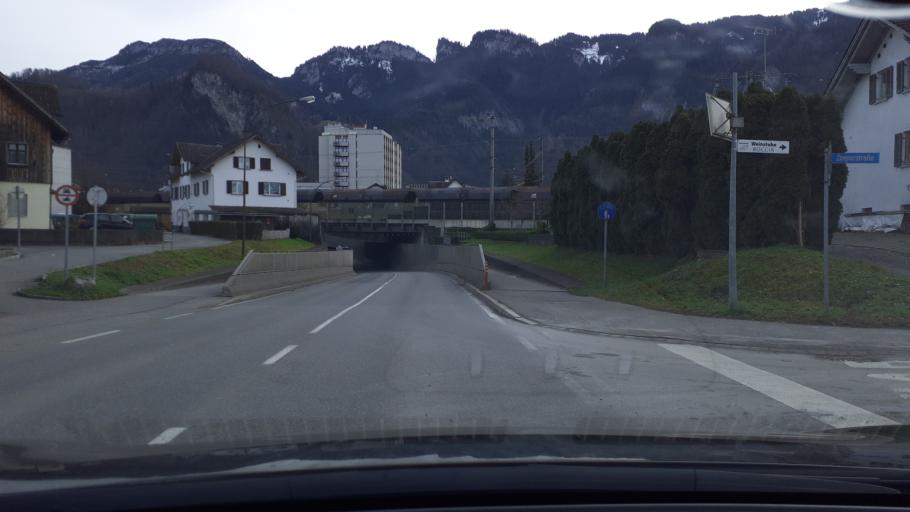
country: AT
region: Vorarlberg
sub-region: Politischer Bezirk Dornbirn
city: Hohenems
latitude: 47.3634
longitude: 9.6776
